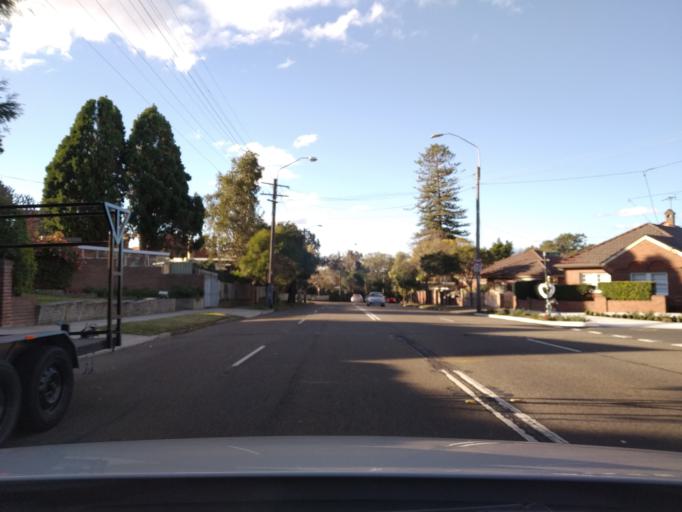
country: AU
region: New South Wales
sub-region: Marrickville
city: Dulwich Hill
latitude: -33.8996
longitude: 151.1332
